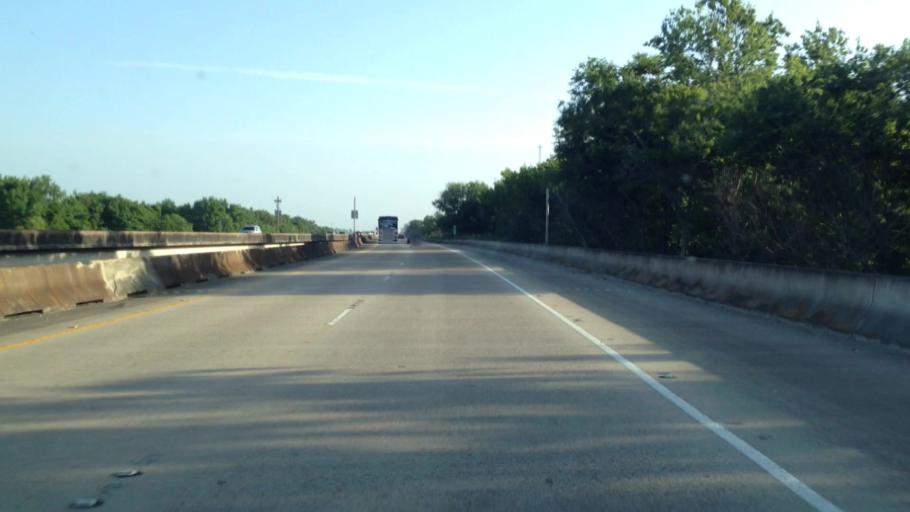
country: US
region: Louisiana
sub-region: Tangipahoa Parish
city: Ponchatoula
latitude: 30.2687
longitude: -90.3985
